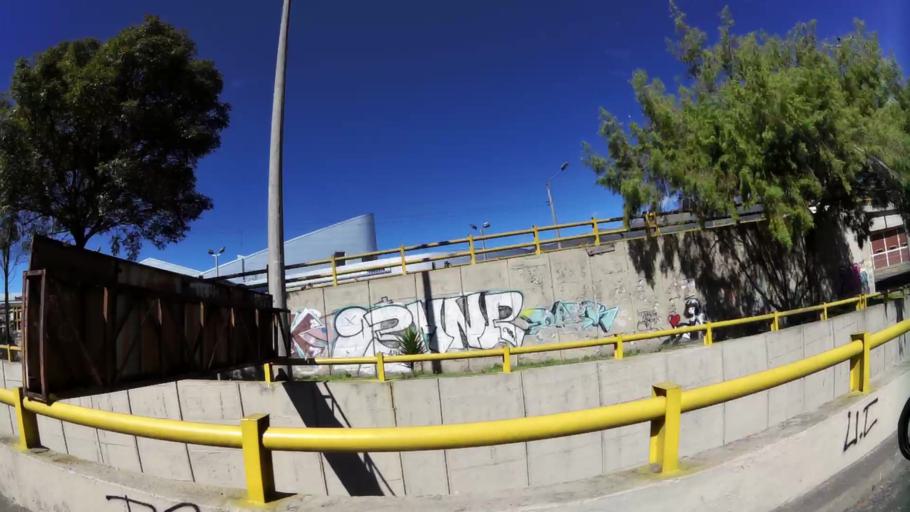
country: EC
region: Pichincha
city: Quito
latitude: -0.1213
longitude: -78.4798
